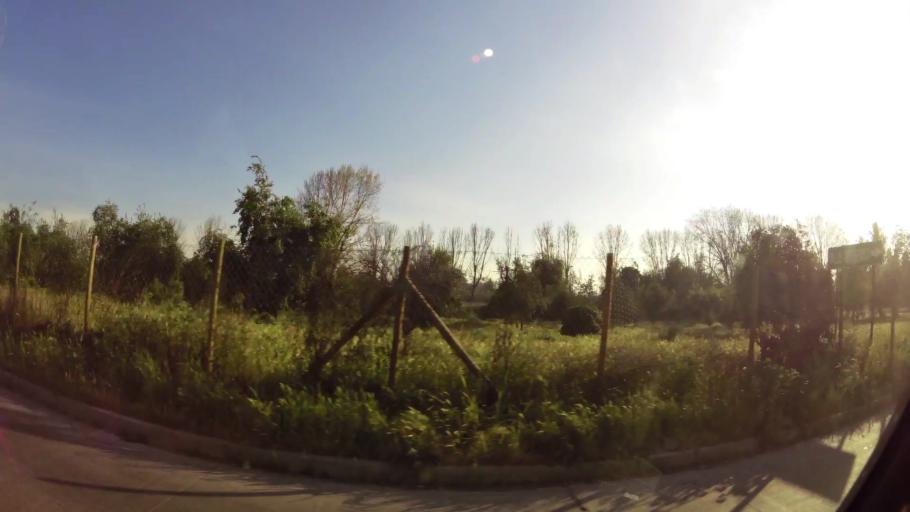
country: CL
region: Santiago Metropolitan
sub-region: Provincia de Santiago
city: Lo Prado
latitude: -33.4501
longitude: -70.7609
